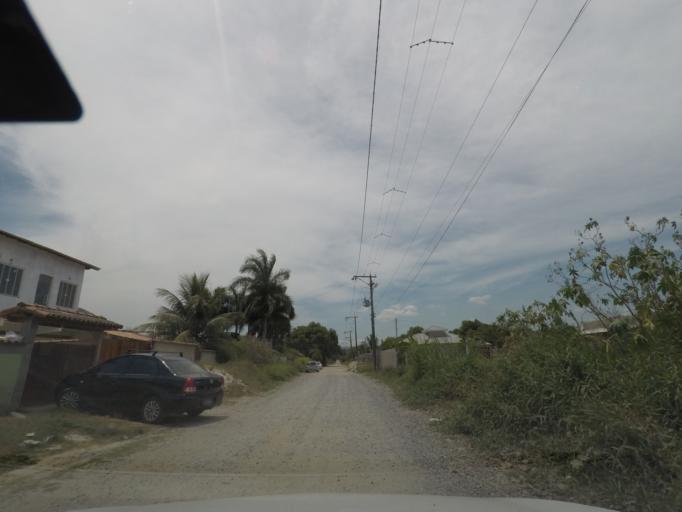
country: BR
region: Rio de Janeiro
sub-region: Marica
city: Marica
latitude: -22.9555
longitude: -42.9456
